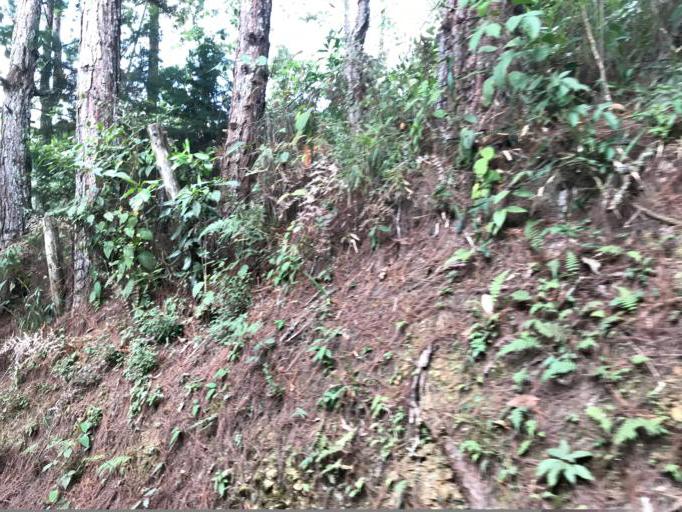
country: CO
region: Valle del Cauca
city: Cali
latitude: 3.4631
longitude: -76.6497
